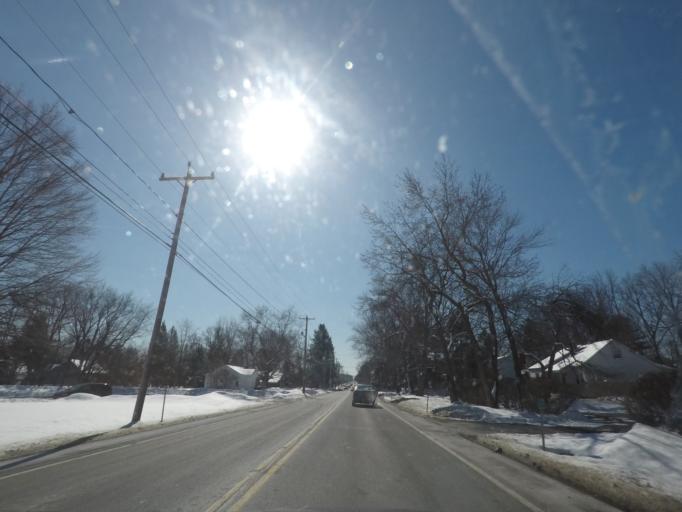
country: US
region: New York
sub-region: Schenectady County
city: Schenectady
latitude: 42.8238
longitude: -73.8922
